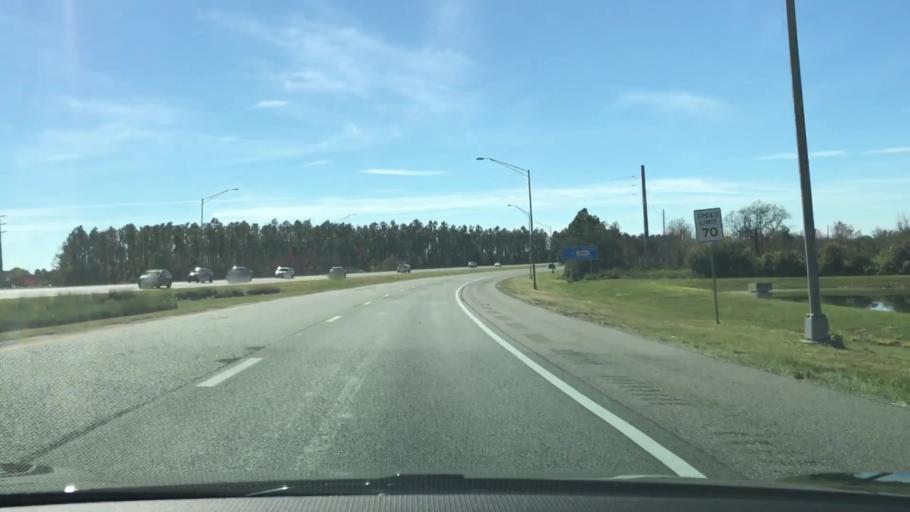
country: US
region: Florida
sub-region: Orange County
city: Gotha
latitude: 28.5335
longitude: -81.5585
